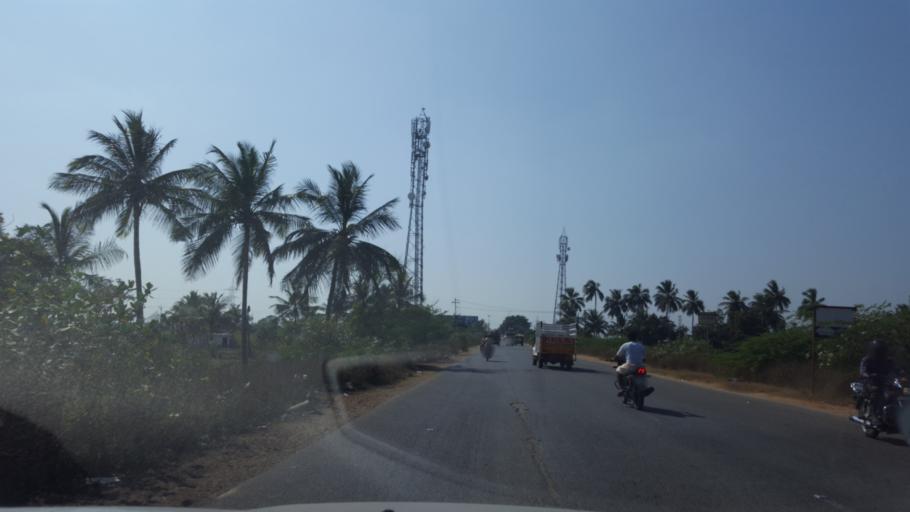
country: IN
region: Tamil Nadu
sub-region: Kancheepuram
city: Kanchipuram
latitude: 12.8681
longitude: 79.6523
